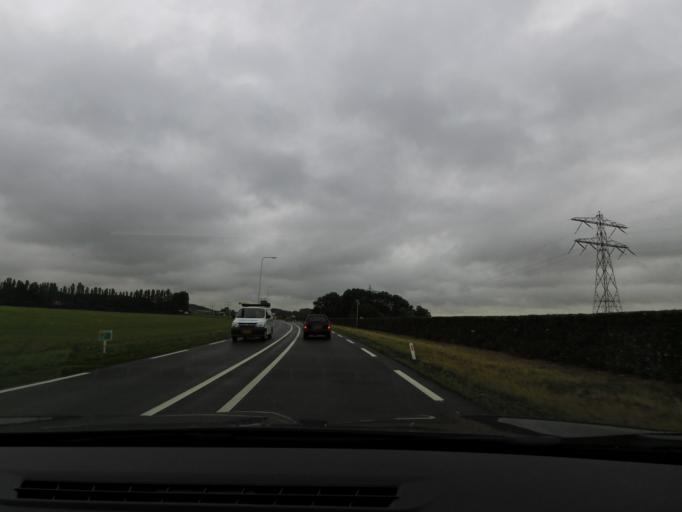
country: NL
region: South Holland
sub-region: Gemeente Maassluis
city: Maassluis
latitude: 51.8633
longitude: 4.2295
